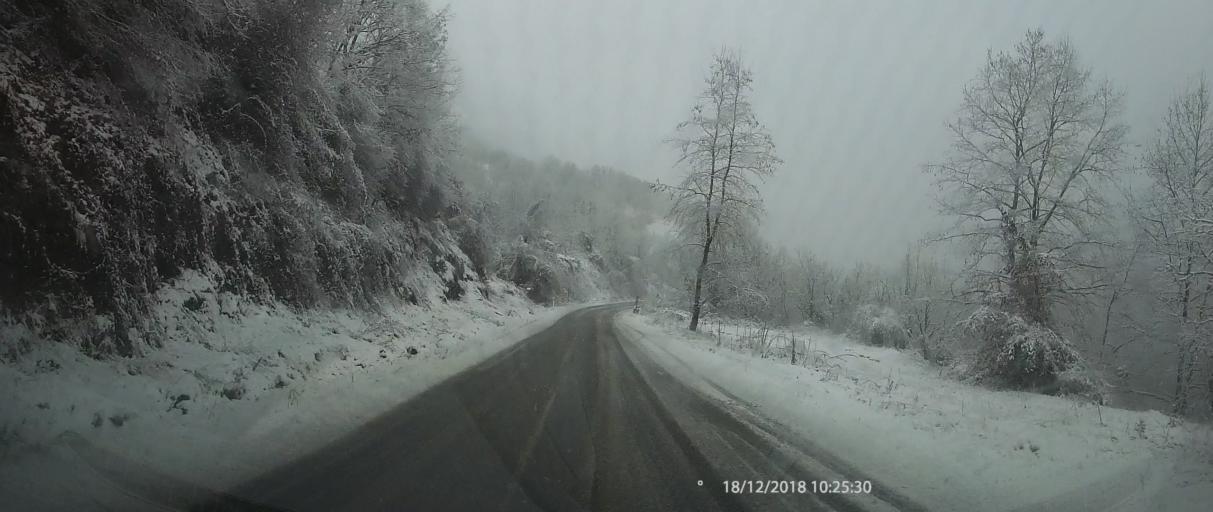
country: GR
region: Thessaly
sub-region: Nomos Larisis
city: Livadi
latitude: 40.1659
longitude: 22.2477
